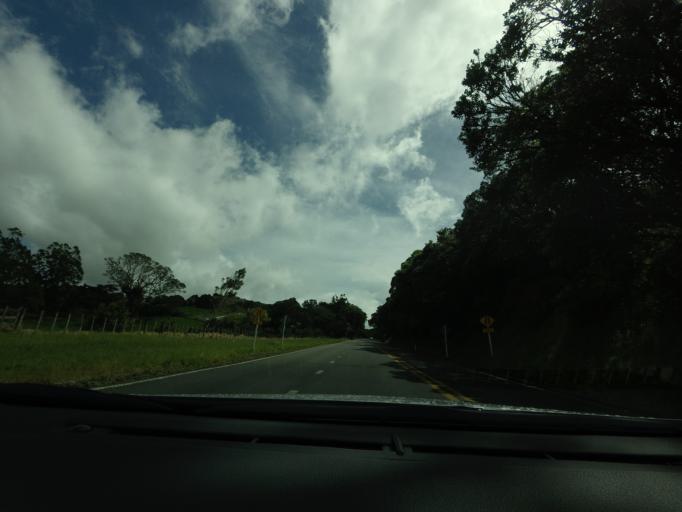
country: NZ
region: Auckland
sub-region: Auckland
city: Warkworth
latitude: -36.5537
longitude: 174.7073
